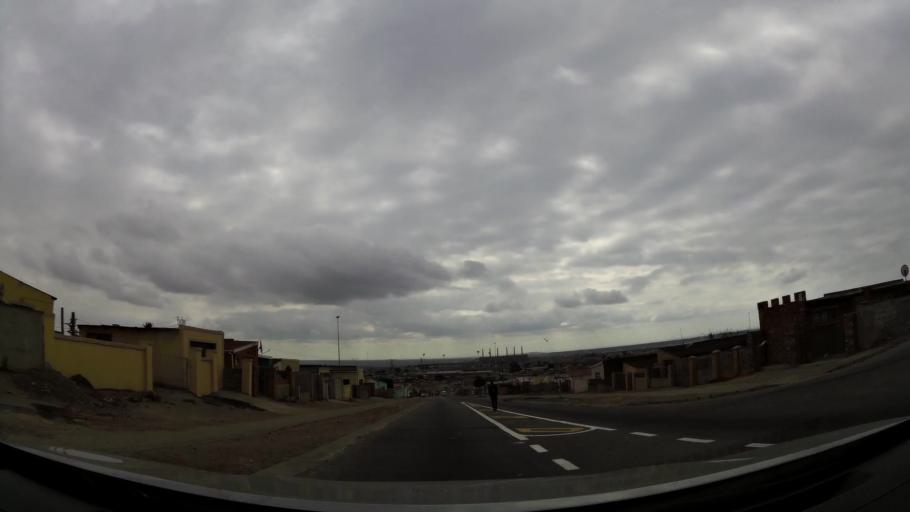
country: ZA
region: Eastern Cape
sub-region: Nelson Mandela Bay Metropolitan Municipality
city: Port Elizabeth
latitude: -33.8910
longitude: 25.5952
